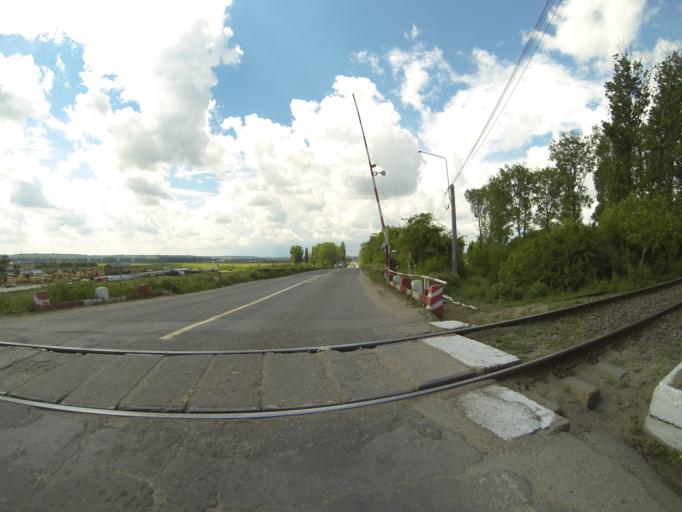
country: RO
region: Dolj
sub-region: Municipiul Craiova
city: Facai
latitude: 44.2765
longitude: 23.8123
